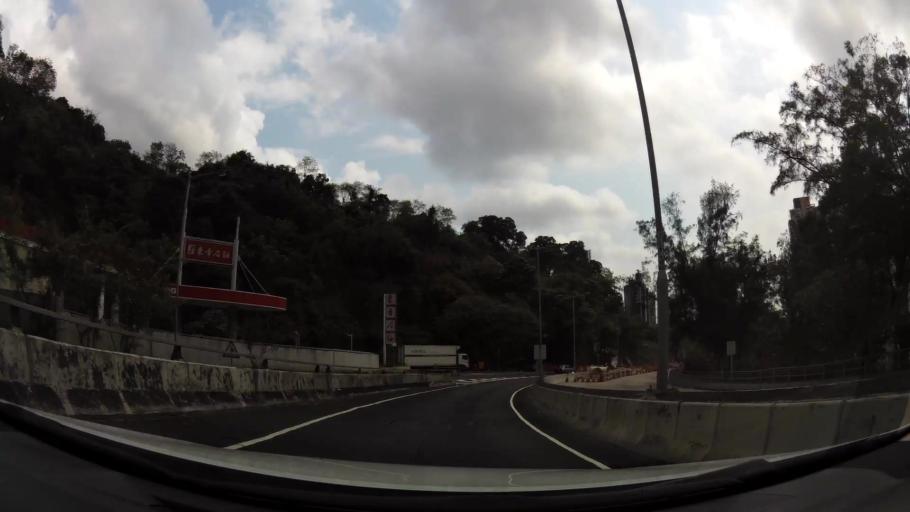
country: HK
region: Sham Shui Po
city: Sham Shui Po
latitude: 22.3388
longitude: 114.1632
